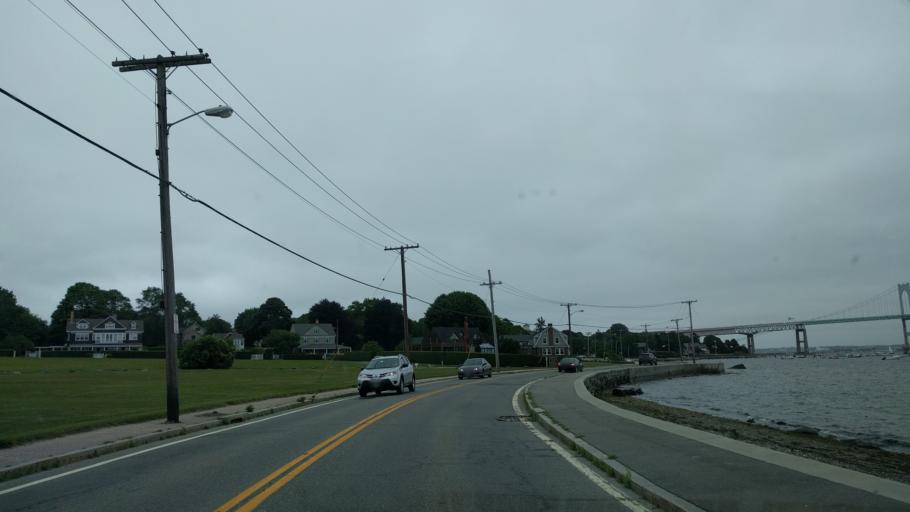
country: US
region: Rhode Island
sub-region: Newport County
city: Jamestown
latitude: 41.4987
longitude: -71.3666
